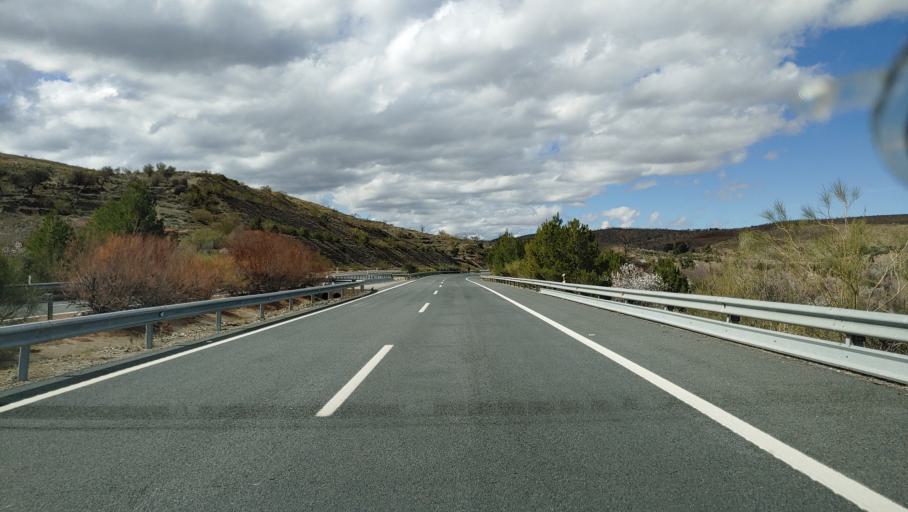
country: ES
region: Andalusia
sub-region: Provincia de Almeria
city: Finana
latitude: 37.1665
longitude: -2.8536
